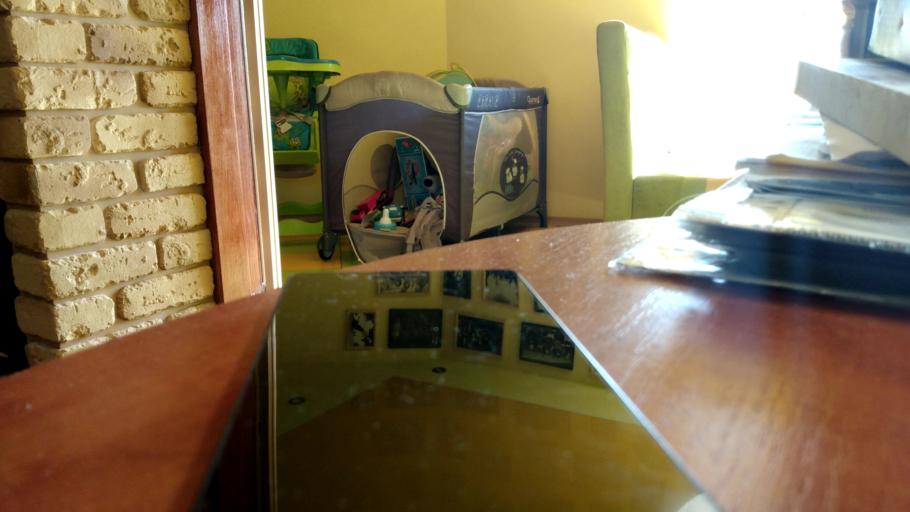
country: RU
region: Penza
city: Serdobsk
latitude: 52.3182
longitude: 44.3853
